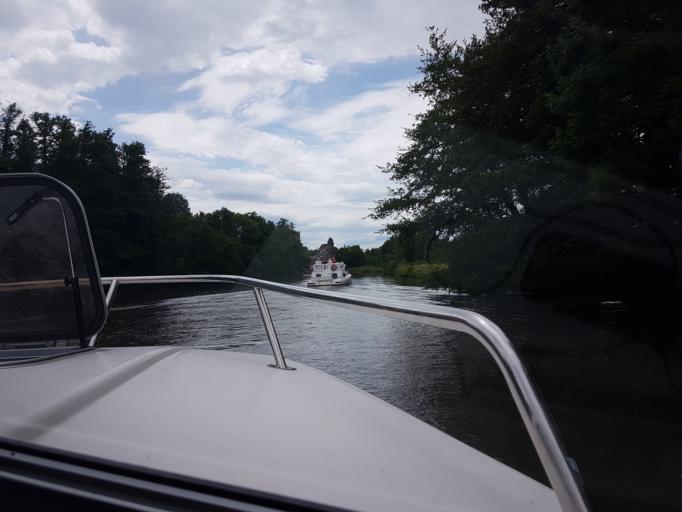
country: FR
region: Bourgogne
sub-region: Departement de la Nievre
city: Clamecy
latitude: 47.4650
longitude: 3.5268
